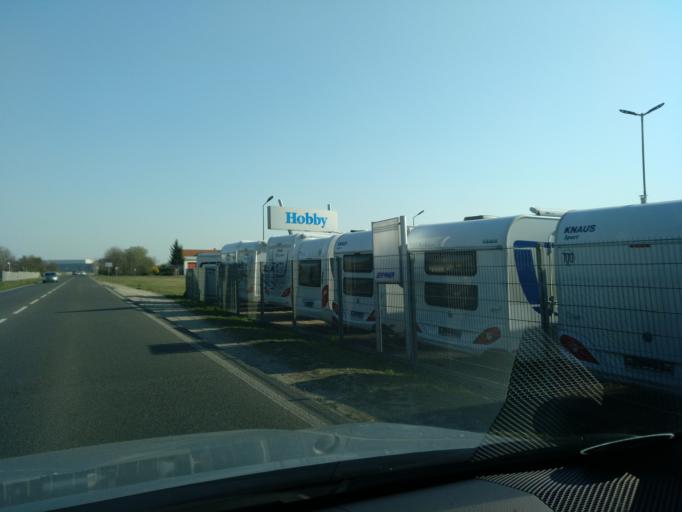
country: DE
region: Brandenburg
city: Hoppegarten
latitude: 52.5025
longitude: 13.6432
